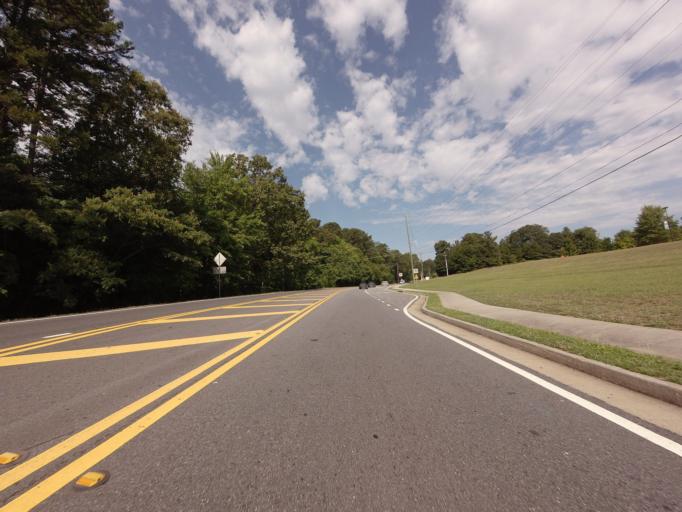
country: US
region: Georgia
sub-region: Fulton County
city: Johns Creek
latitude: 34.0550
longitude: -84.1971
